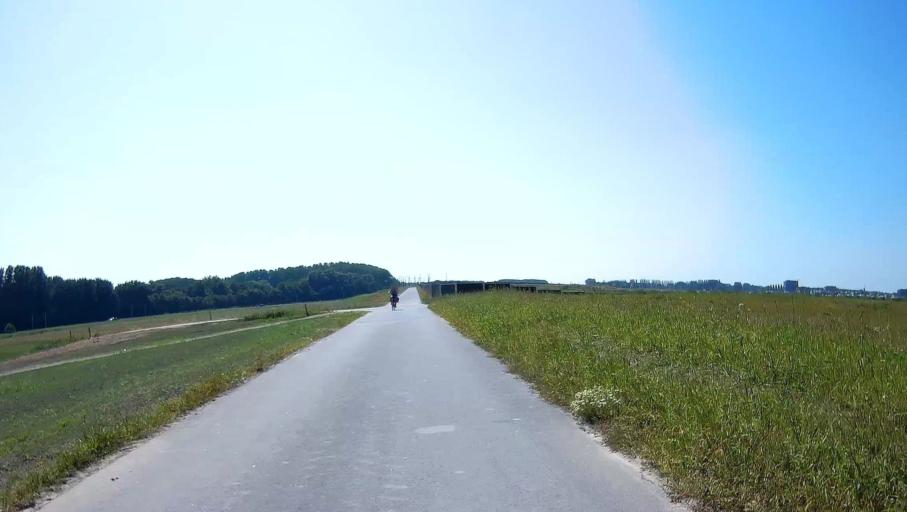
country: NL
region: South Holland
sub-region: Gemeente Pijnacker-Nootdorp
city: Pijnacker
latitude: 52.0615
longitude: 4.4426
